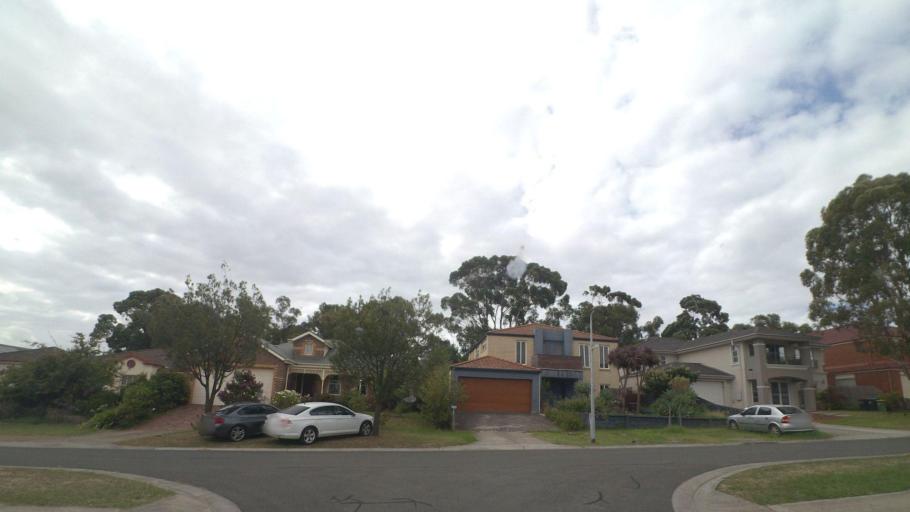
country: AU
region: Victoria
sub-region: Knox
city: Wantirna South
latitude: -37.8855
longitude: 145.2172
